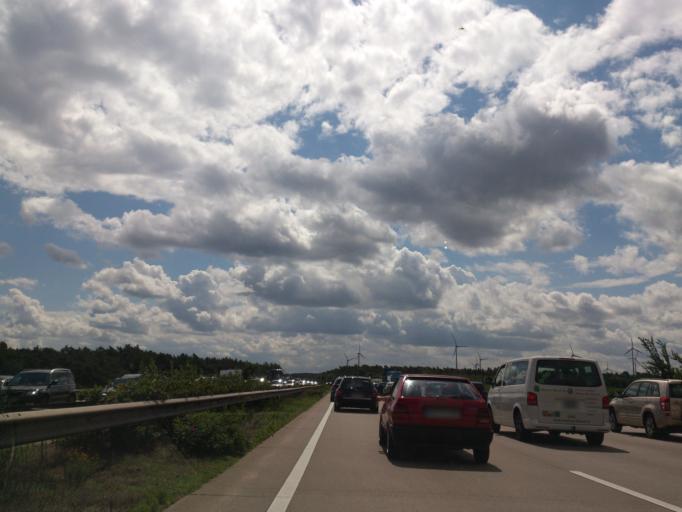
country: DE
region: Lower Saxony
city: Elze
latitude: 52.5960
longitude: 9.7502
